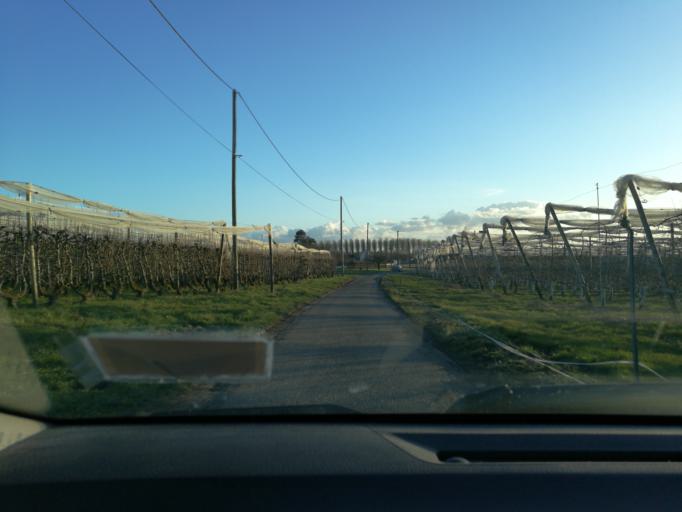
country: FR
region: Centre
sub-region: Departement du Loiret
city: Semoy
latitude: 47.9403
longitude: 1.9649
